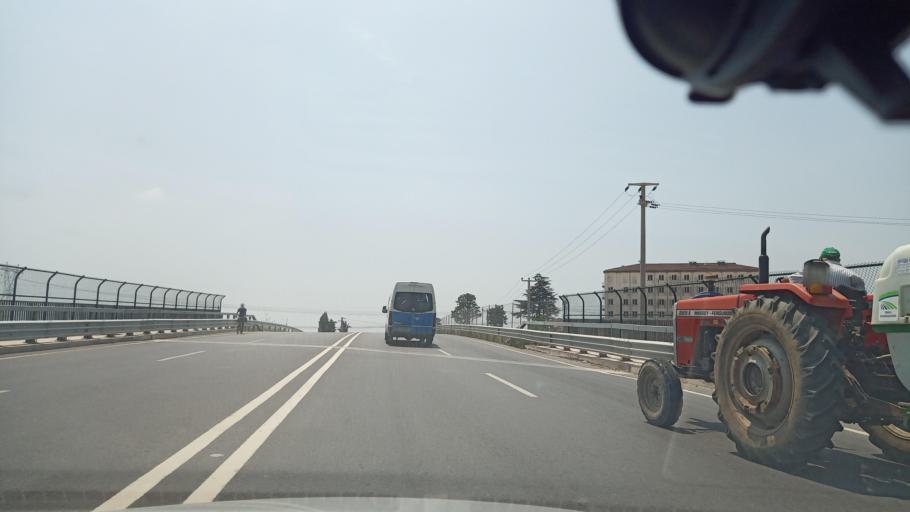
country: TR
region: Sakarya
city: Adapazari
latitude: 40.8247
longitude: 30.3967
